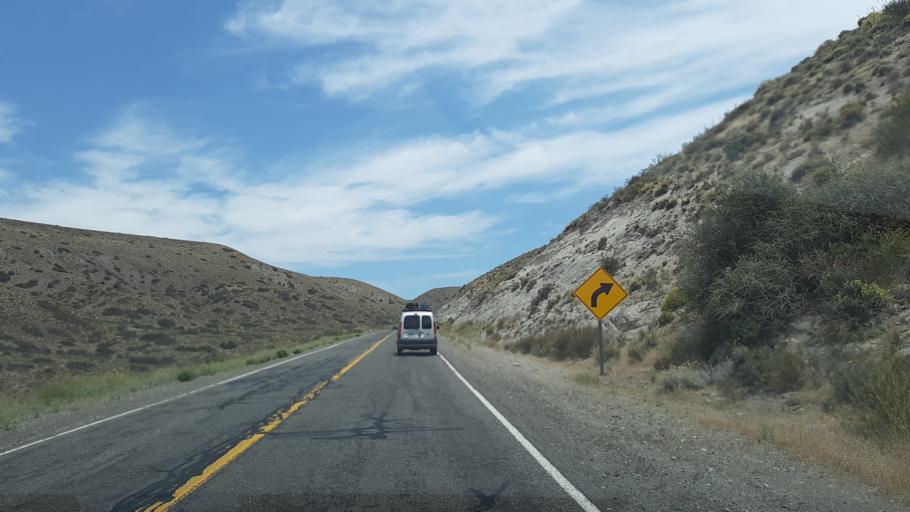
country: AR
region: Rio Negro
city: Pilcaniyeu
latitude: -40.4715
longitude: -70.6585
